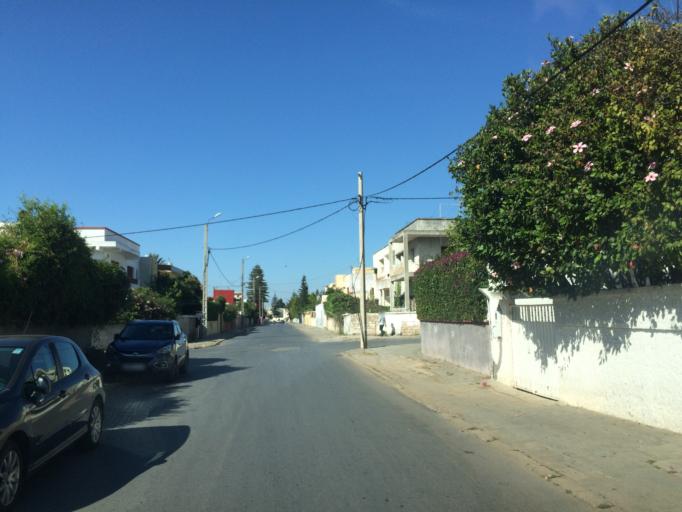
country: MA
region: Rabat-Sale-Zemmour-Zaer
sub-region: Rabat
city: Rabat
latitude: 33.9889
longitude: -6.8212
